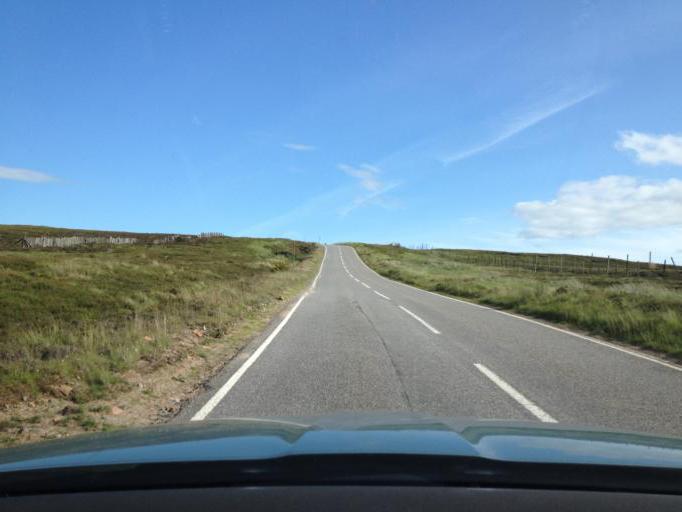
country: GB
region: Scotland
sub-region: Aberdeenshire
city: Laurencekirk
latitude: 56.9186
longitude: -2.5789
